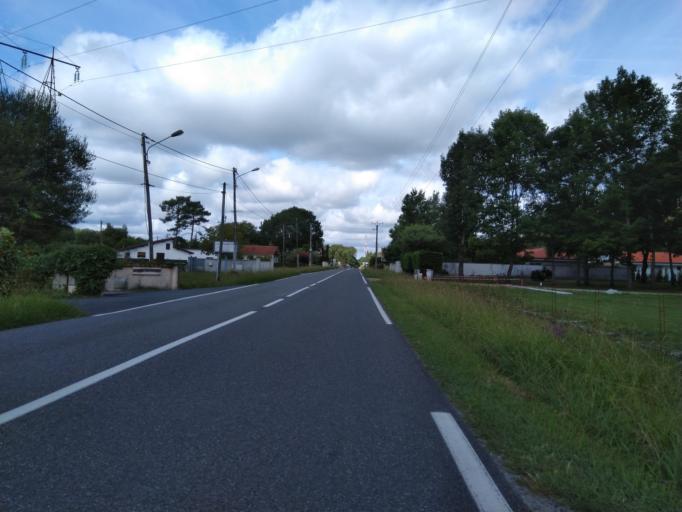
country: FR
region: Aquitaine
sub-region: Departement des Landes
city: Mees
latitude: 43.7313
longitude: -1.0972
